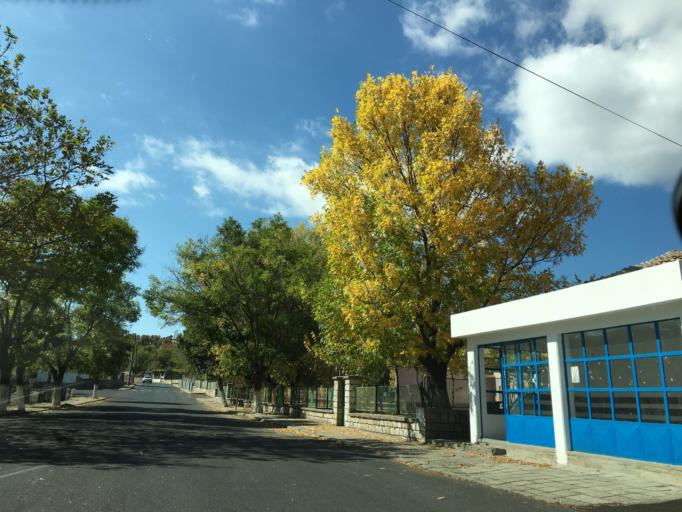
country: BG
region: Kurdzhali
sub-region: Obshtina Kurdzhali
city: Kurdzhali
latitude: 41.5450
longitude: 25.4921
